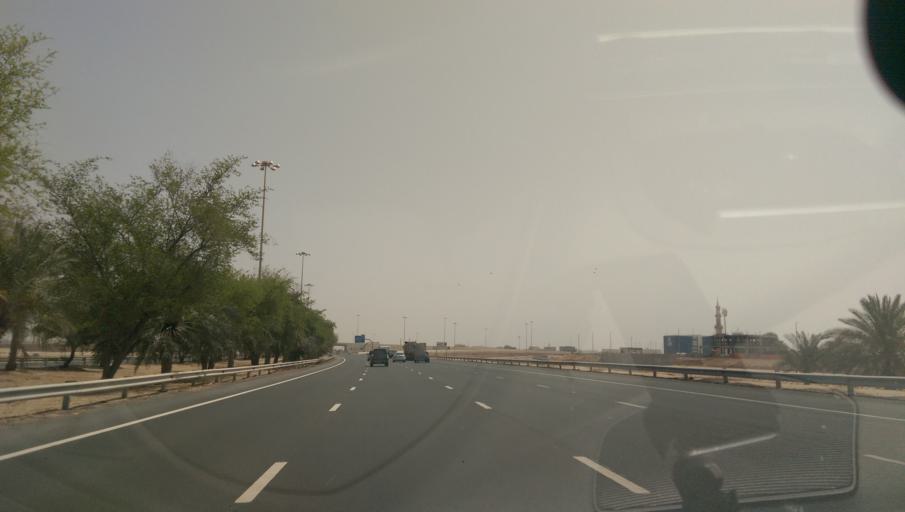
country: AE
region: Abu Dhabi
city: Abu Dhabi
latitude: 24.3348
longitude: 54.6333
